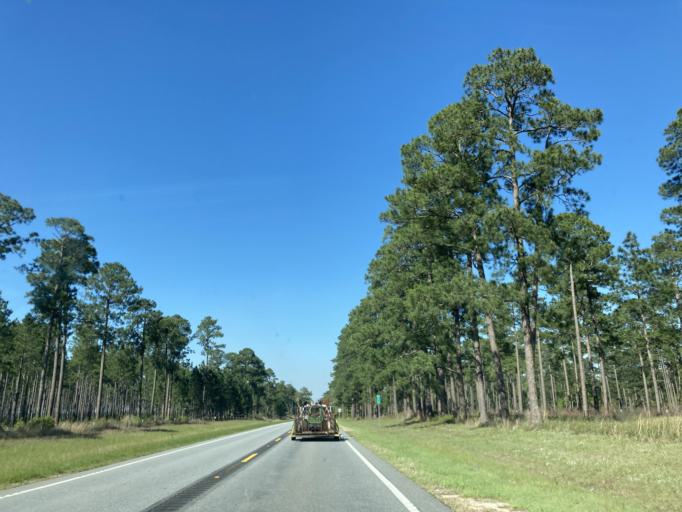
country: US
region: Georgia
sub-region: Baker County
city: Newton
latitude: 31.3552
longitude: -84.2988
